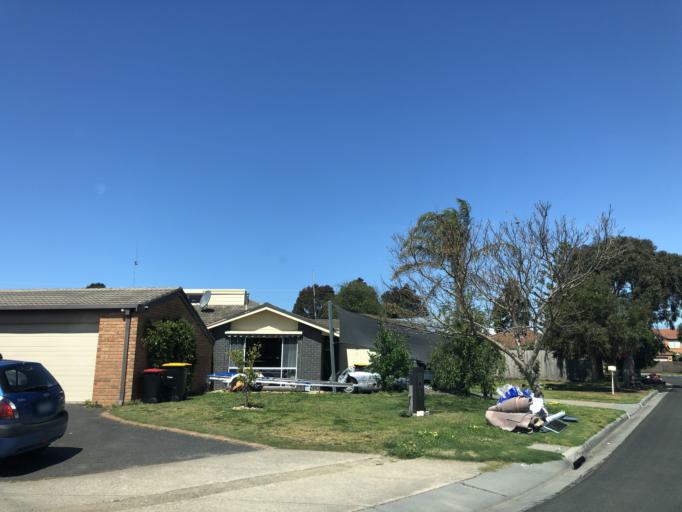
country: AU
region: Victoria
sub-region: Kingston
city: Patterson Lakes
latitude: -38.0784
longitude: 145.1418
